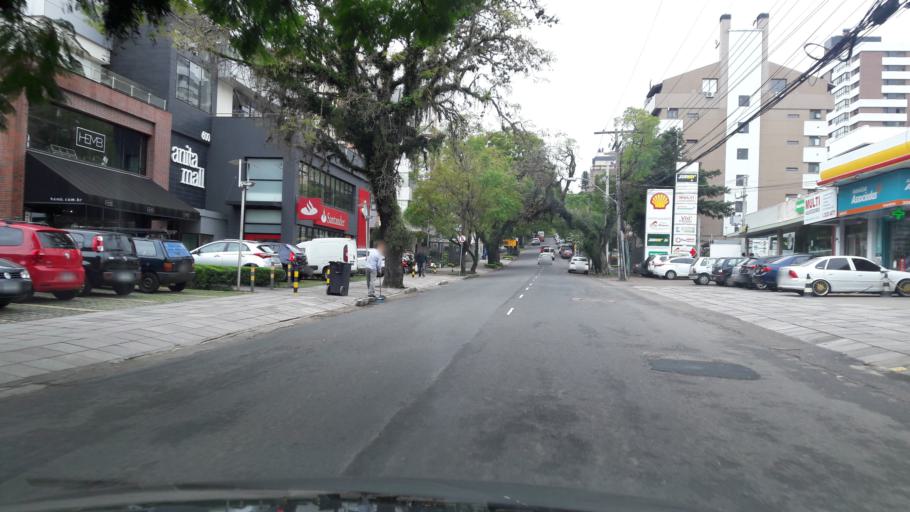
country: BR
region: Rio Grande do Sul
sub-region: Porto Alegre
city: Porto Alegre
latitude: -30.0269
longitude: -51.1899
